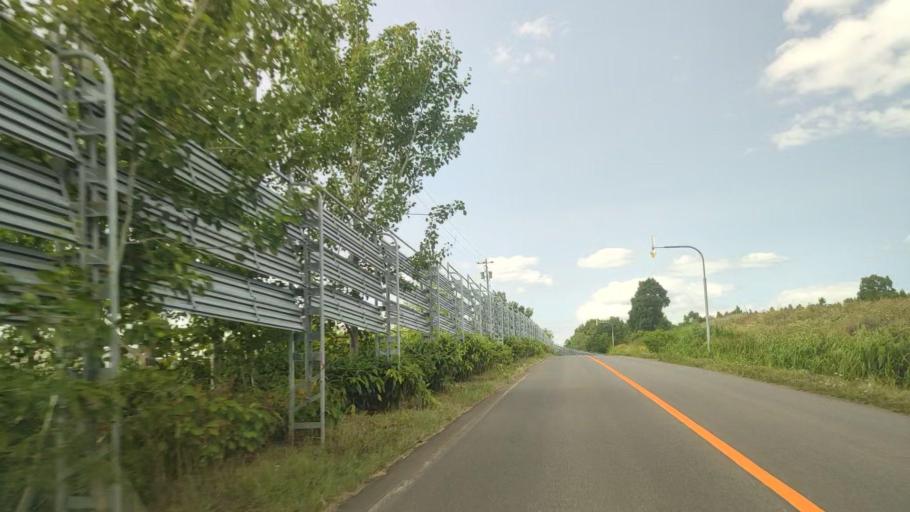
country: JP
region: Hokkaido
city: Nayoro
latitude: 44.2469
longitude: 142.4156
